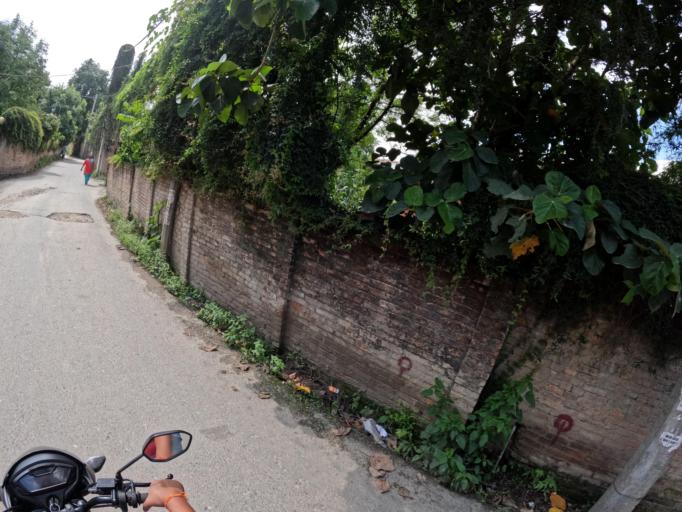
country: NP
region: Central Region
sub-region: Bagmati Zone
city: Patan
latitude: 27.6815
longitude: 85.3079
